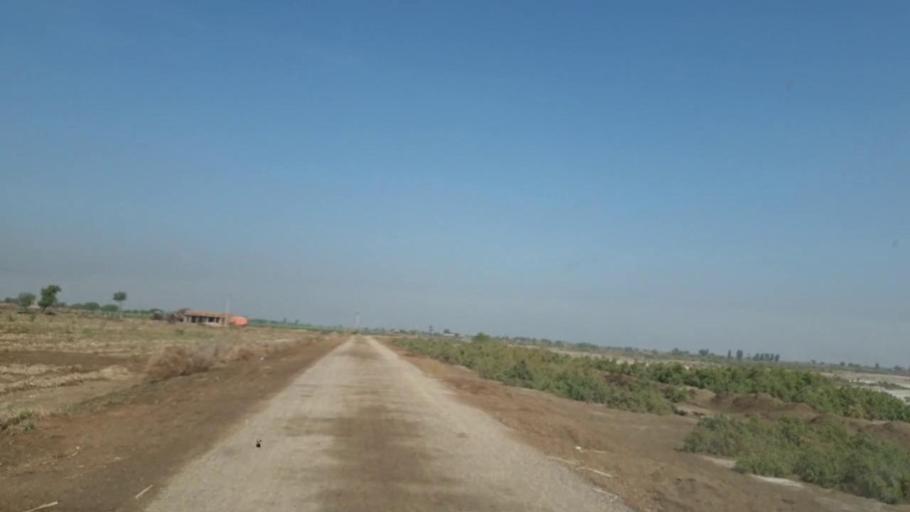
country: PK
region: Sindh
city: Mirpur Khas
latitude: 25.5669
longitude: 69.1850
